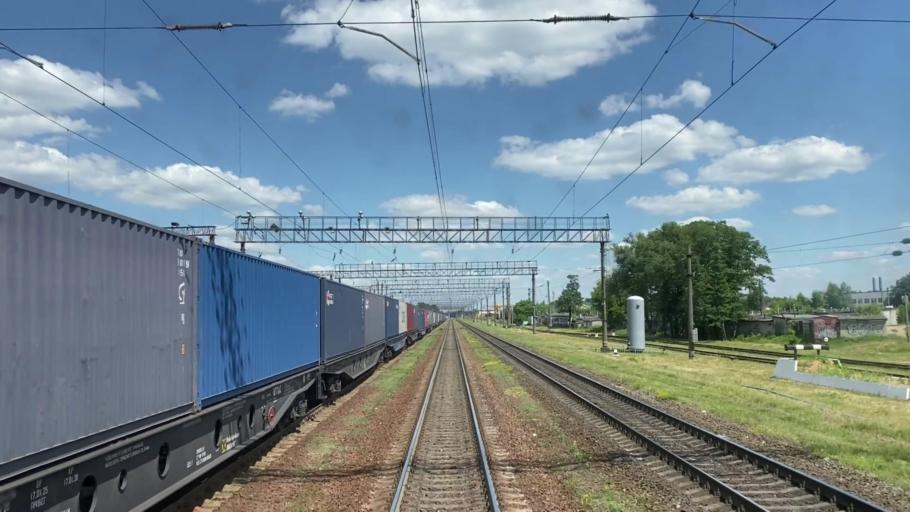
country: BY
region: Brest
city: Brest
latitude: 52.1145
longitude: 23.7524
